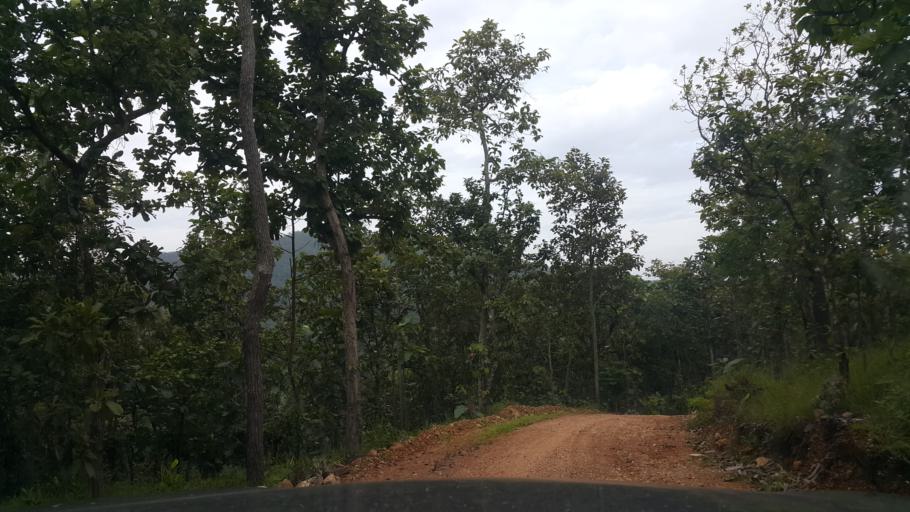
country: TH
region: Chiang Mai
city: San Sai
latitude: 18.9605
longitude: 99.1297
